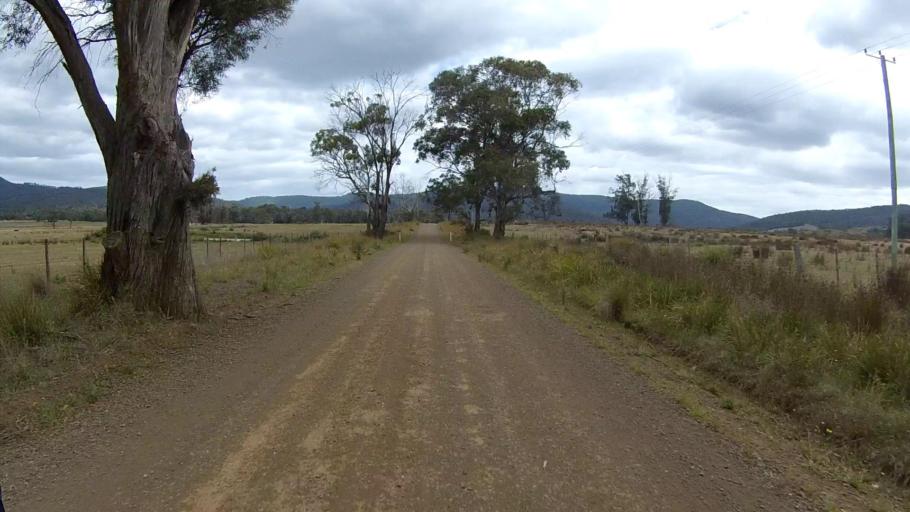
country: AU
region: Tasmania
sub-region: Sorell
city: Sorell
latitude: -42.6336
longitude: 147.9203
